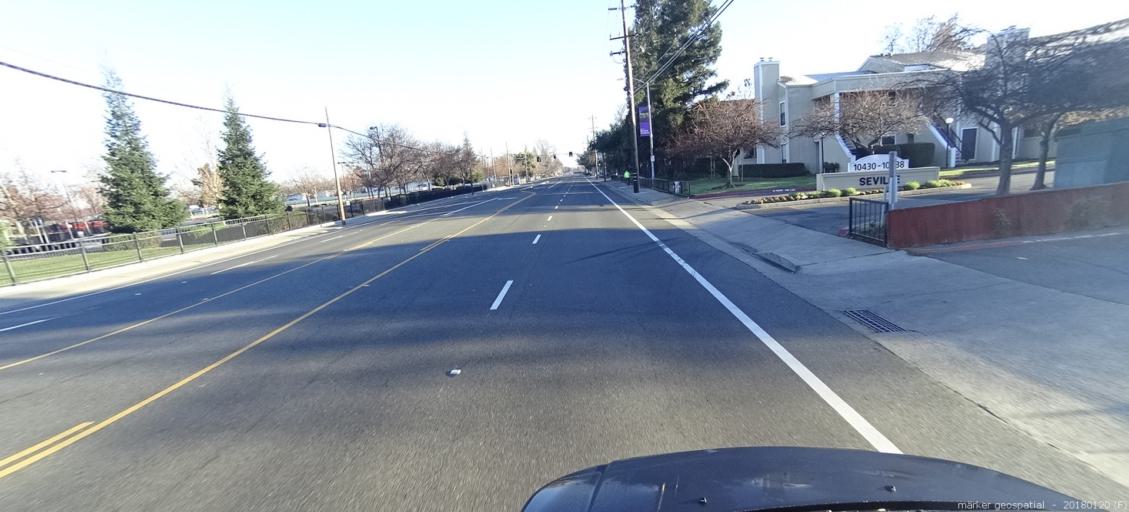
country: US
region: California
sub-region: Sacramento County
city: Rancho Cordova
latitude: 38.5982
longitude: -121.3032
